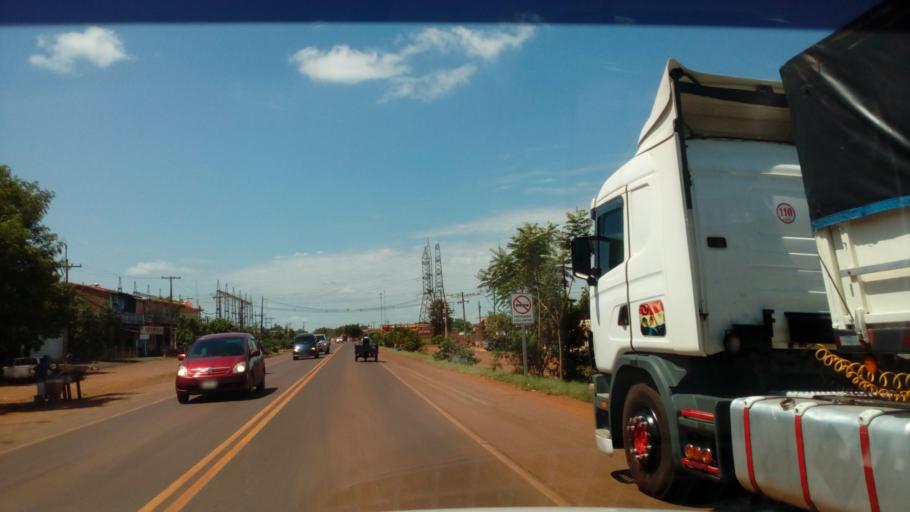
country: PY
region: Alto Parana
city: Colonia Yguazu
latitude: -25.4858
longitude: -54.8976
